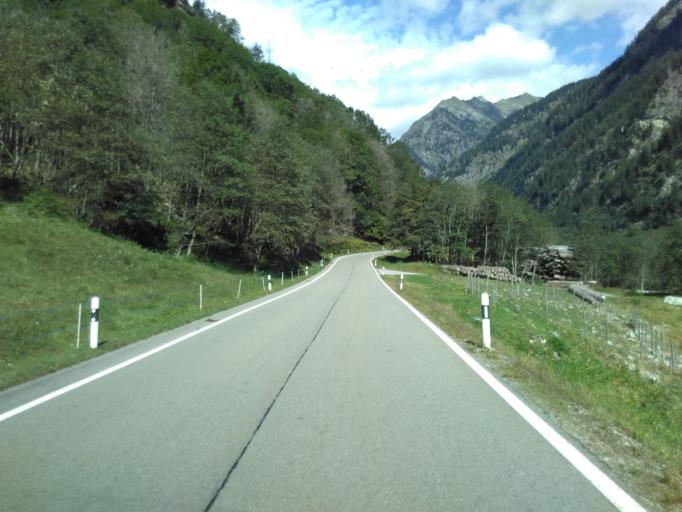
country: CH
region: Grisons
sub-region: Moesa District
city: Cauco
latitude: 46.3459
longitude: 9.1195
